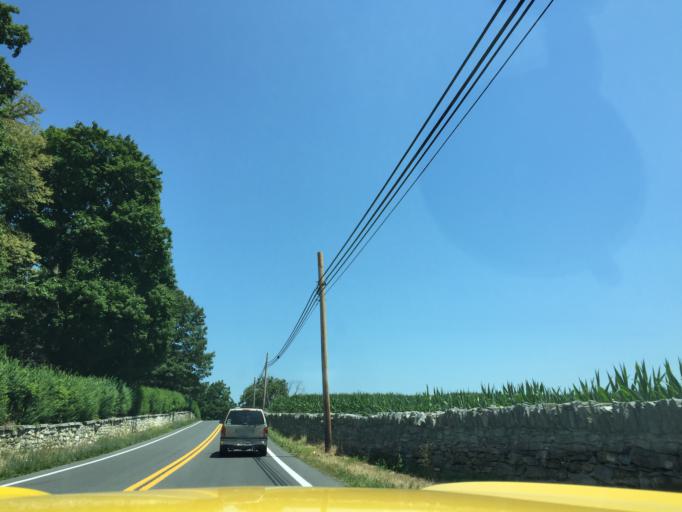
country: US
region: West Virginia
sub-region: Jefferson County
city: Ranson
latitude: 39.2895
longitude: -77.8825
